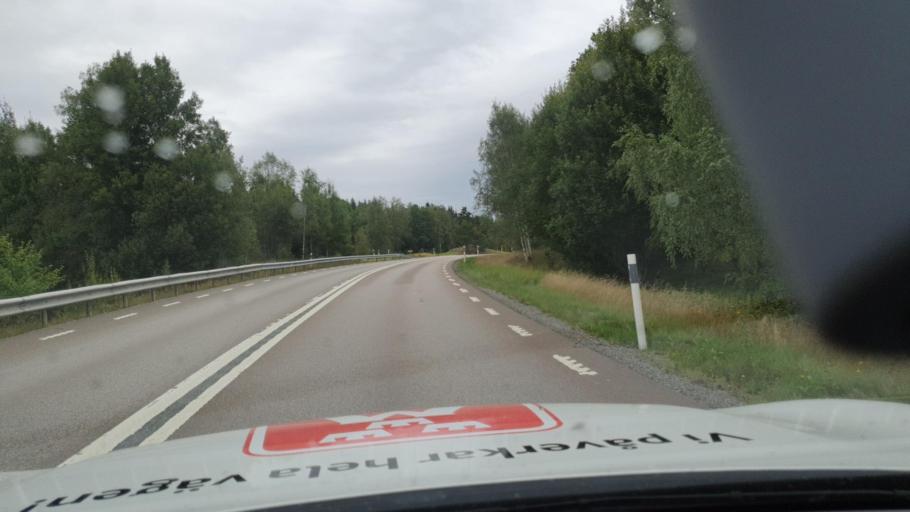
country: SE
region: Vaestra Goetaland
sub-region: Dals-Ed Kommun
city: Ed
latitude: 58.9196
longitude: 12.0232
